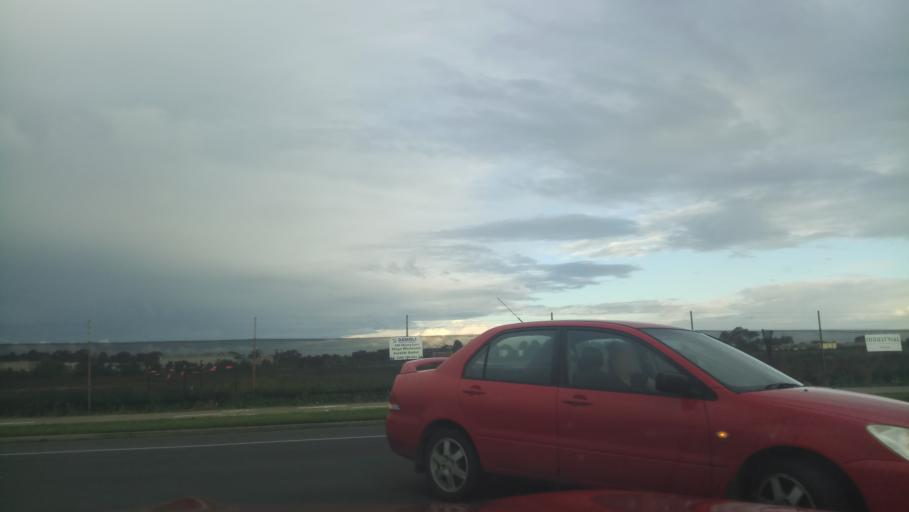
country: AU
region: Victoria
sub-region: Hobsons Bay
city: Williamstown North
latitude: -37.8514
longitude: 144.8678
